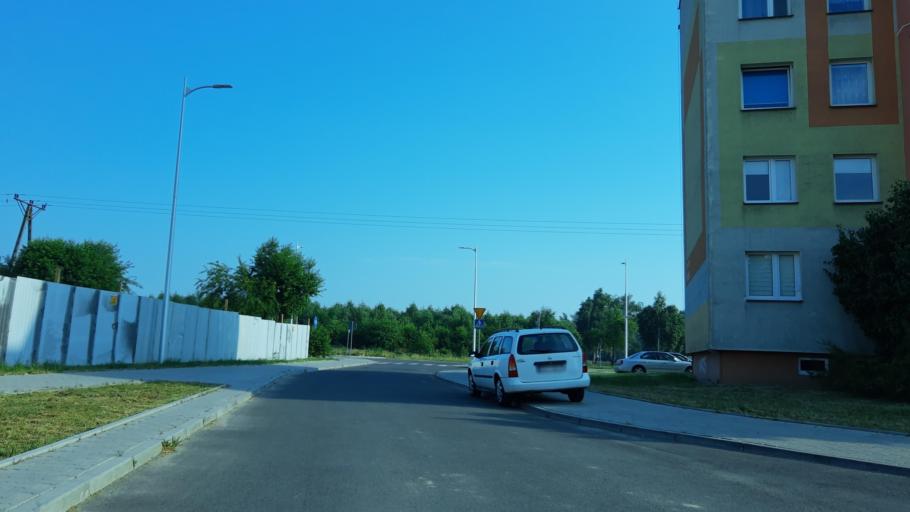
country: PL
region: Lodz Voivodeship
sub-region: Powiat sieradzki
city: Sieradz
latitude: 51.5850
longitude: 18.7083
